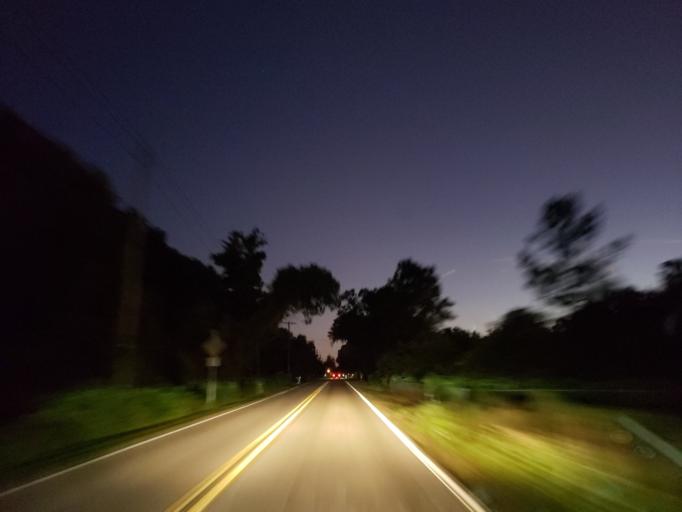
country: US
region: Florida
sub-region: Hillsborough County
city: Dover
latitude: 28.0019
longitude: -82.2199
